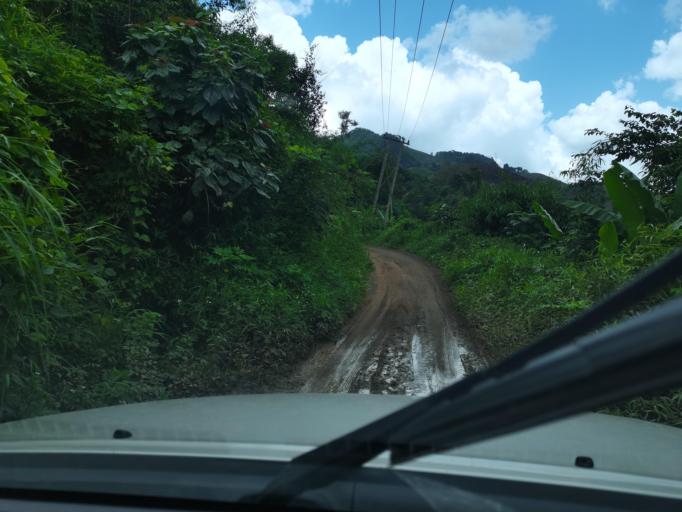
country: LA
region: Loungnamtha
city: Muang Long
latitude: 20.7684
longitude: 101.0170
